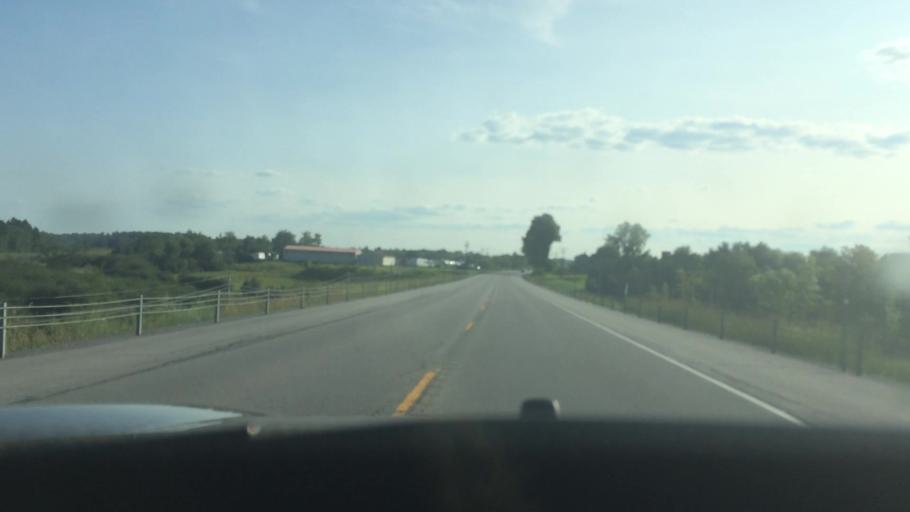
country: US
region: New York
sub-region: St. Lawrence County
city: Potsdam
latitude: 44.6614
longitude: -75.0340
